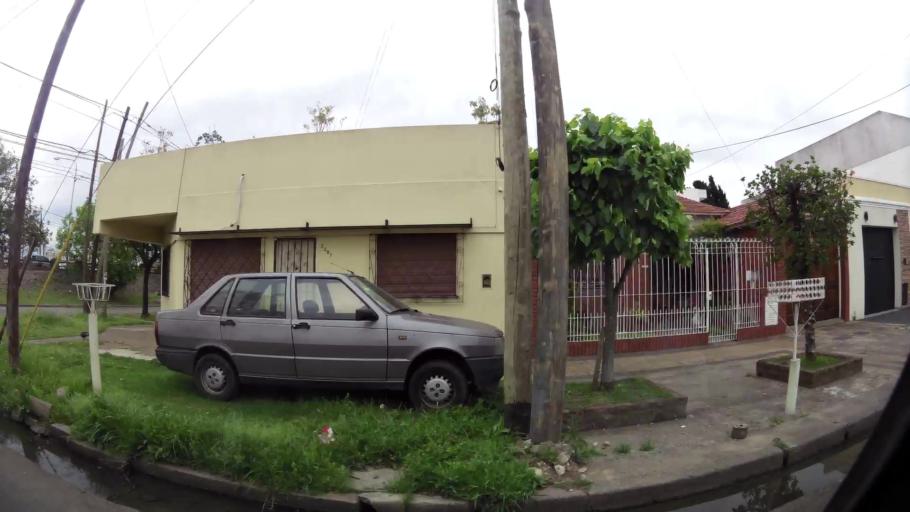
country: AR
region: Buenos Aires
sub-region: Partido de Lanus
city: Lanus
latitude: -34.6887
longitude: -58.3802
